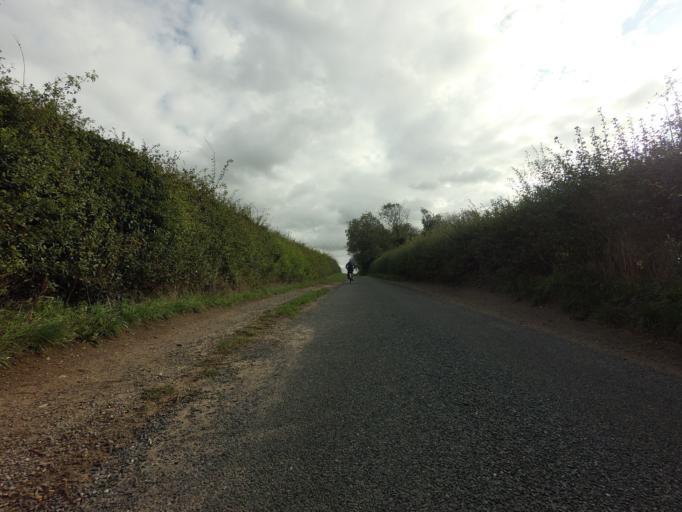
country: GB
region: England
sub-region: Norfolk
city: Dersingham
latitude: 52.8609
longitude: 0.5123
